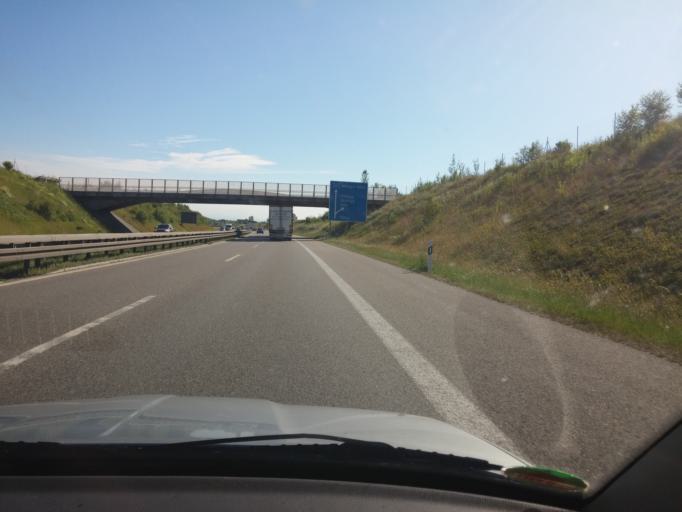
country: DE
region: Baden-Wuerttemberg
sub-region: Tuebingen Region
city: Kisslegg
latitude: 47.7602
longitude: 9.9139
